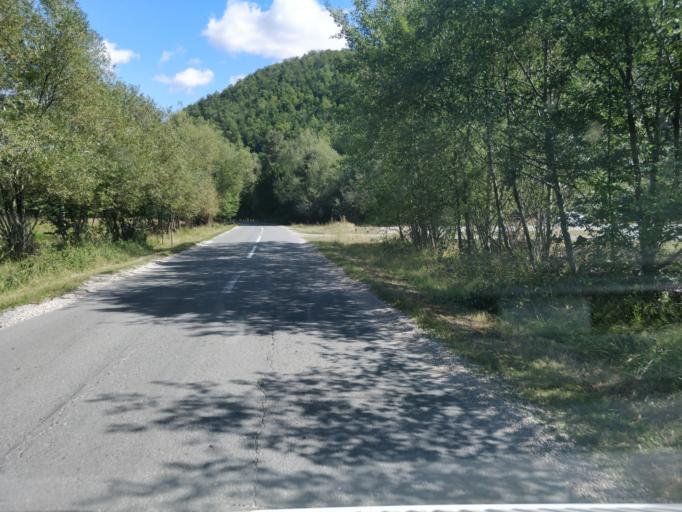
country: RO
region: Cluj
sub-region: Comuna Sacueu
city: Sacuieu
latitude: 46.8465
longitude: 22.8619
